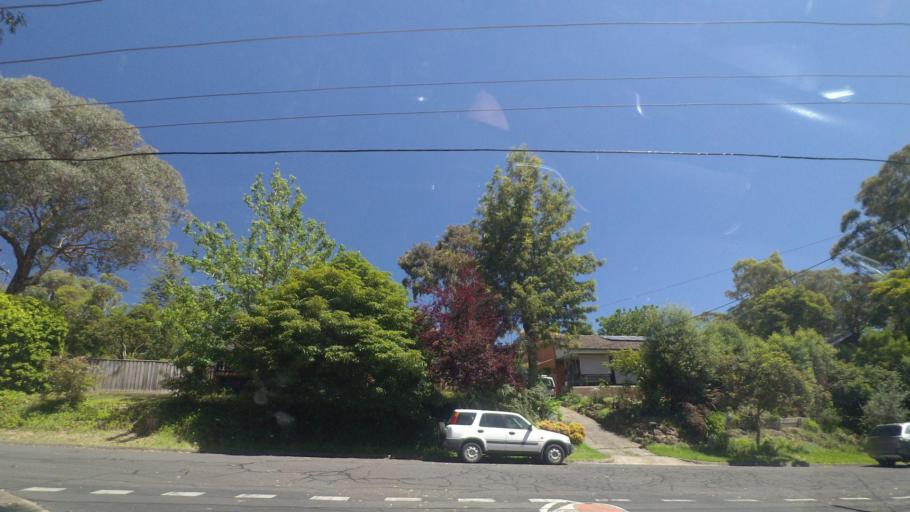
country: AU
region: Victoria
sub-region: Manningham
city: Park Orchards
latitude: -37.8002
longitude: 145.2278
